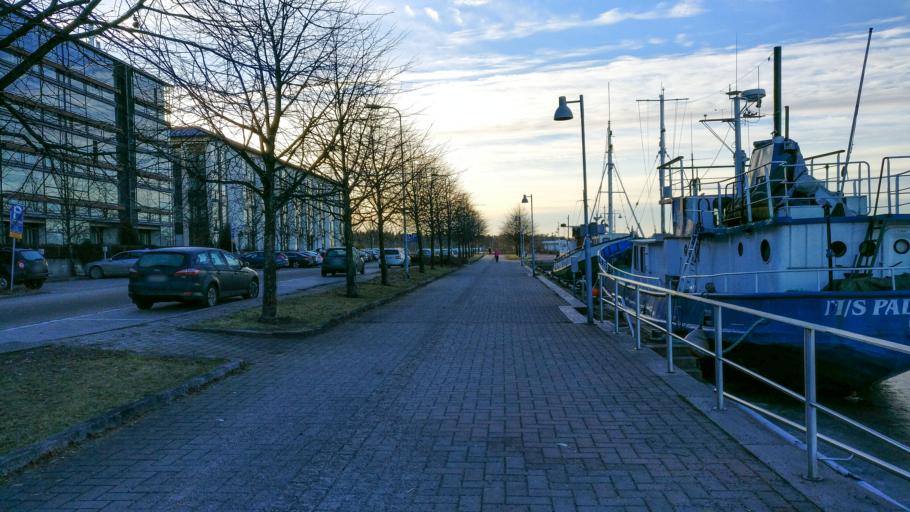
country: FI
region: Uusimaa
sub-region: Helsinki
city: Helsinki
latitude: 60.1870
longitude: 25.0301
